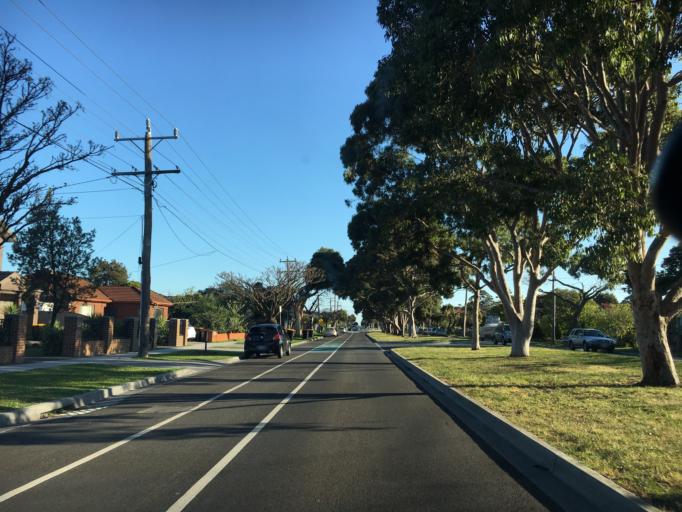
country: AU
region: Victoria
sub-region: Kingston
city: Clayton South
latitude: -37.9333
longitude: 145.1278
